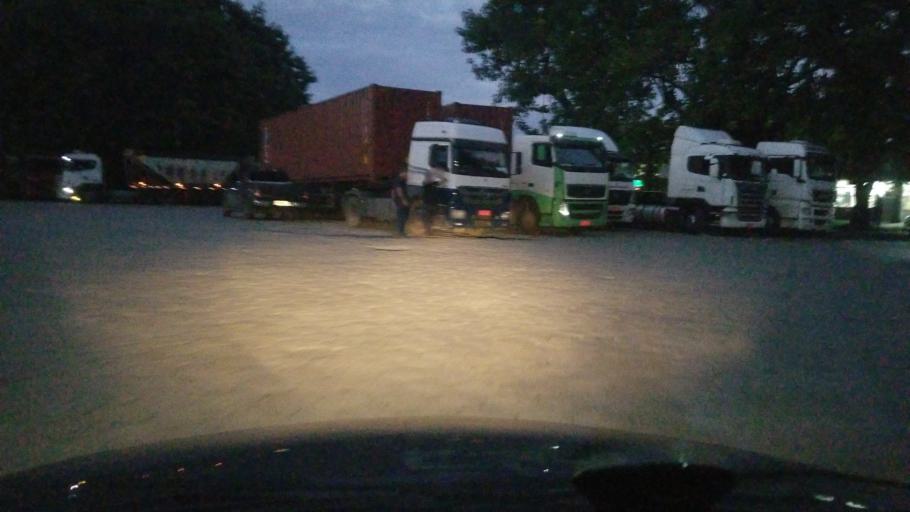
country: BR
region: Sao Paulo
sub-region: Sao Vicente
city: Sao Vicente
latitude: -23.9263
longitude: -46.3849
